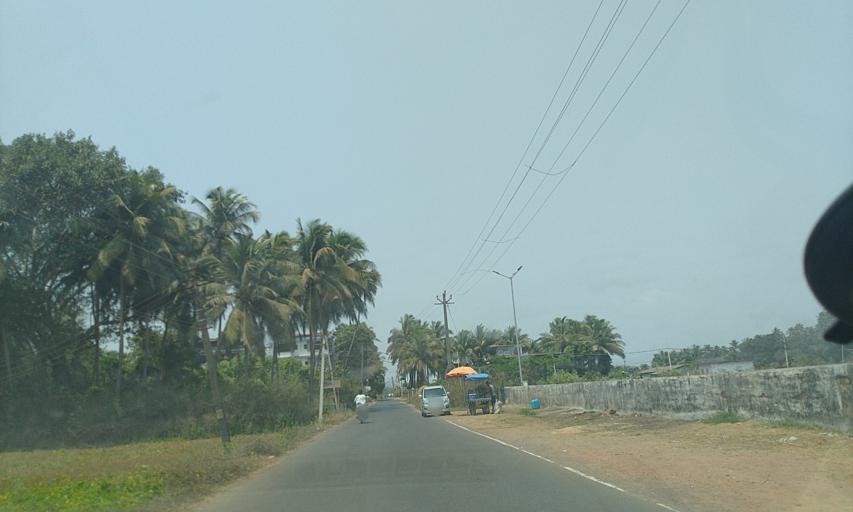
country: IN
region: Goa
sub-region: North Goa
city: Saligao
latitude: 15.5520
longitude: 73.8064
